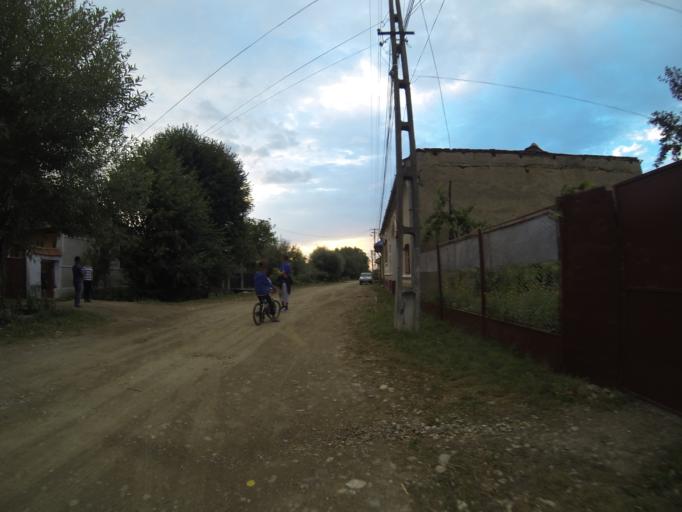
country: RO
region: Brasov
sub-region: Comuna Sinca Veche
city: Sinca Veche
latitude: 45.7643
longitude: 25.1751
